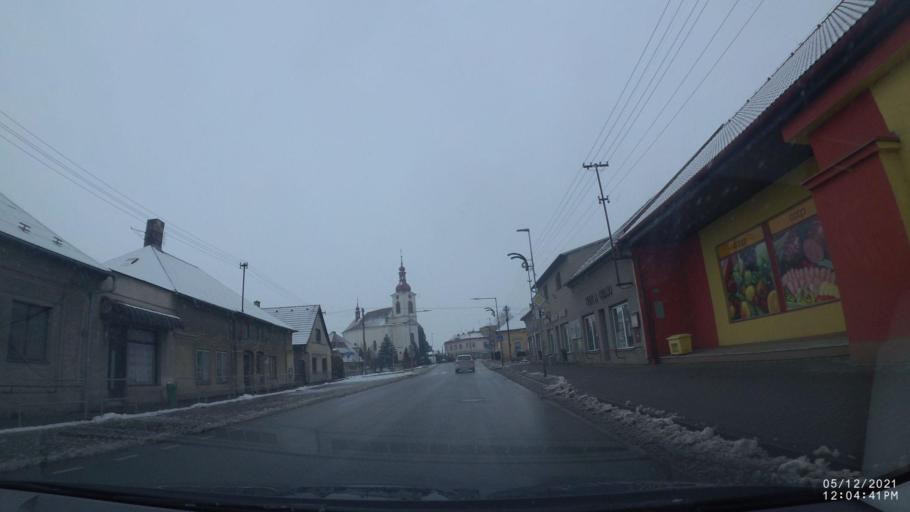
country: CZ
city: Ceske Mezirici
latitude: 50.2859
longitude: 16.0460
